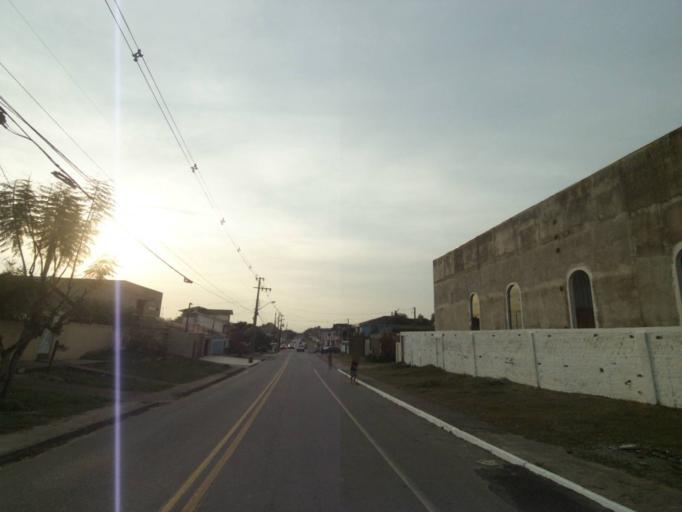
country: BR
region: Parana
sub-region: Paranagua
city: Paranagua
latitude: -25.5255
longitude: -48.5332
